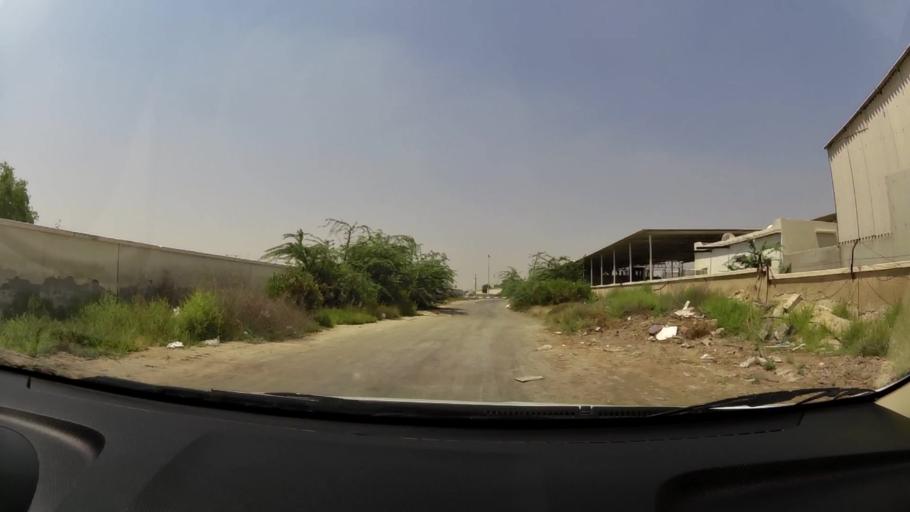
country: AE
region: Umm al Qaywayn
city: Umm al Qaywayn
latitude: 25.5565
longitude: 55.5537
